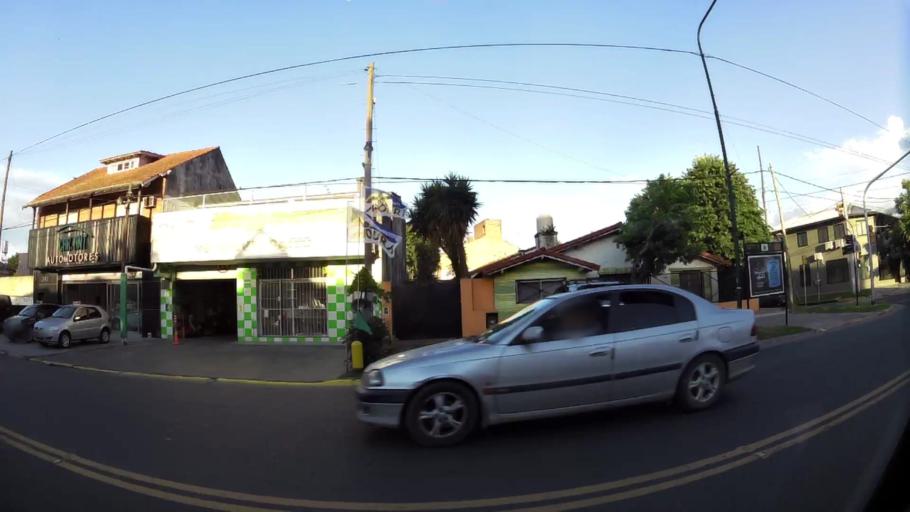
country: AR
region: Buenos Aires
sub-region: Partido de San Isidro
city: San Isidro
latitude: -34.4797
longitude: -58.5288
